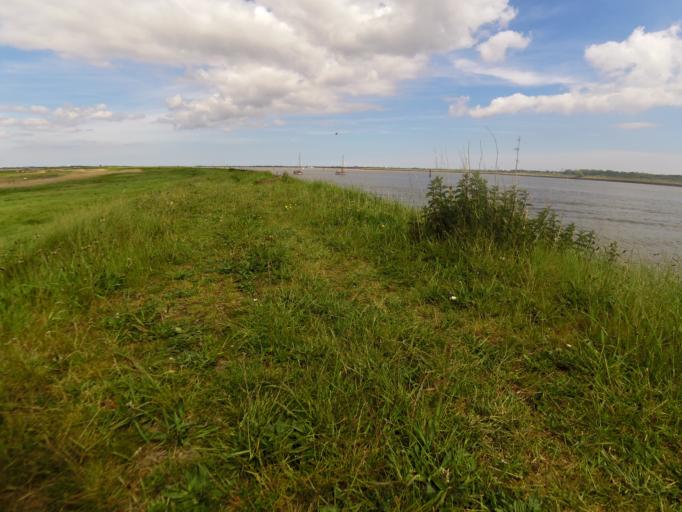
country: GB
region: England
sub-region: Norfolk
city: Great Yarmouth
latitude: 52.5958
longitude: 1.6498
